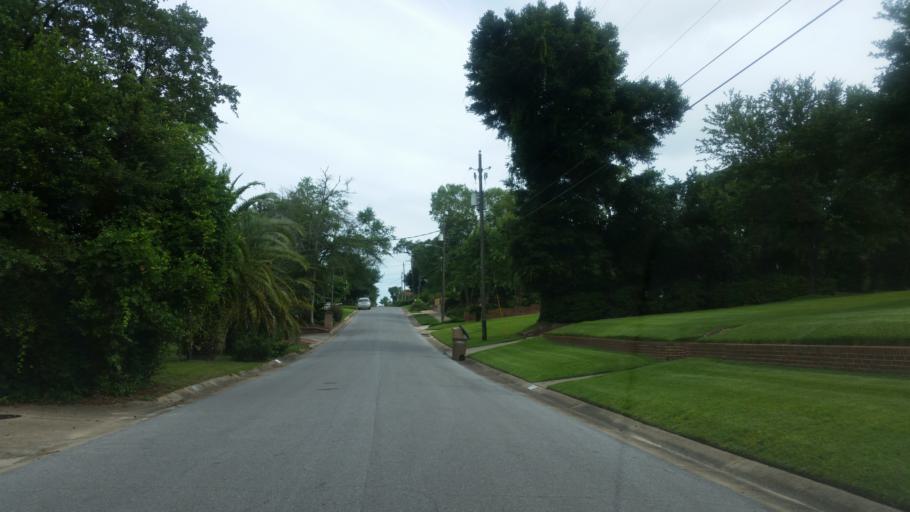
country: US
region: Florida
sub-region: Escambia County
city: East Pensacola Heights
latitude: 30.4381
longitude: -87.1901
